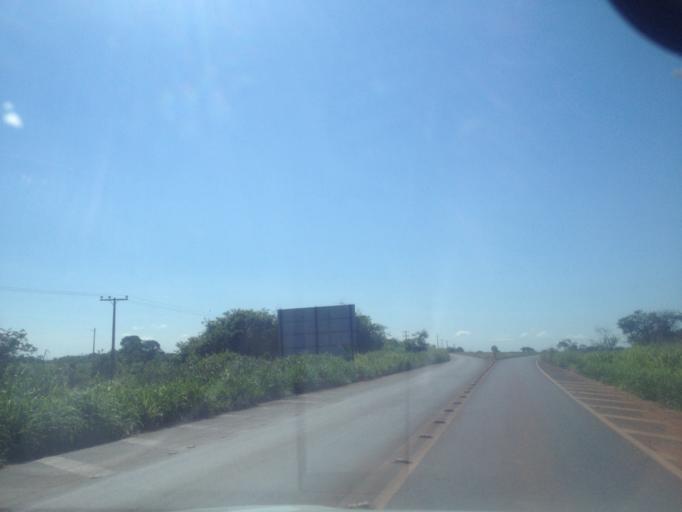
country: BR
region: Minas Gerais
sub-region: Santa Vitoria
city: Santa Vitoria
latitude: -18.9891
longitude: -50.5750
